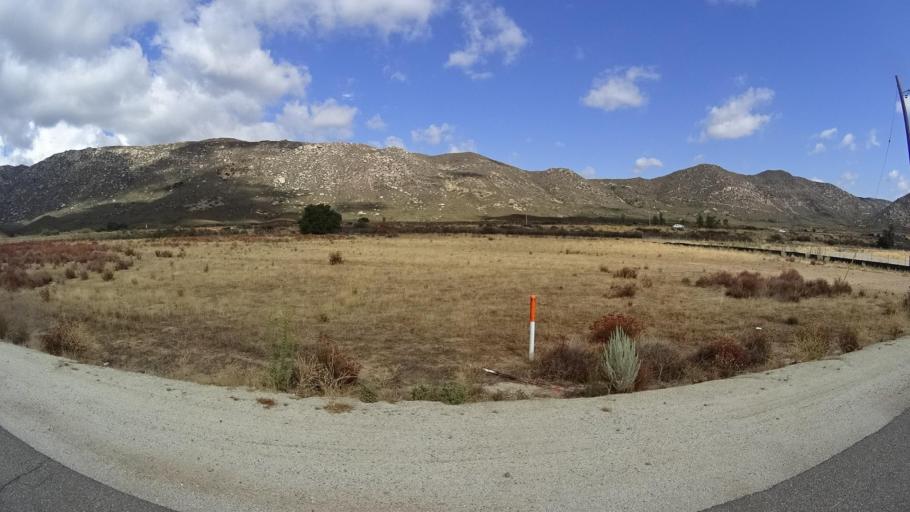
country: US
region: California
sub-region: San Diego County
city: Pine Valley
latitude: 32.7632
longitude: -116.4890
